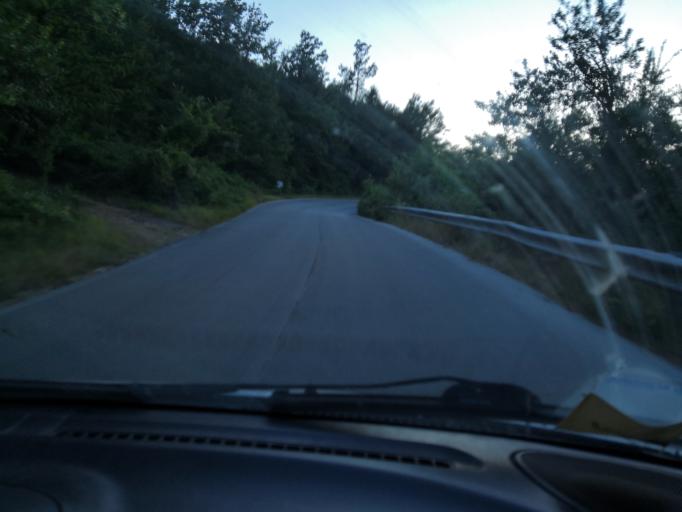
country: IT
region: Molise
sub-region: Provincia di Campobasso
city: Jelsi
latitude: 41.5106
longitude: 14.7830
